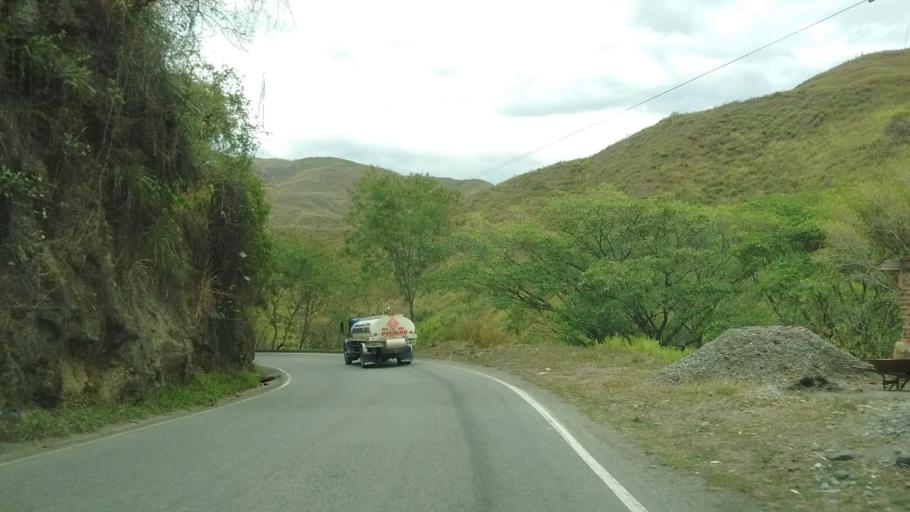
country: CO
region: Cauca
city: La Sierra
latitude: 2.1970
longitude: -76.8209
